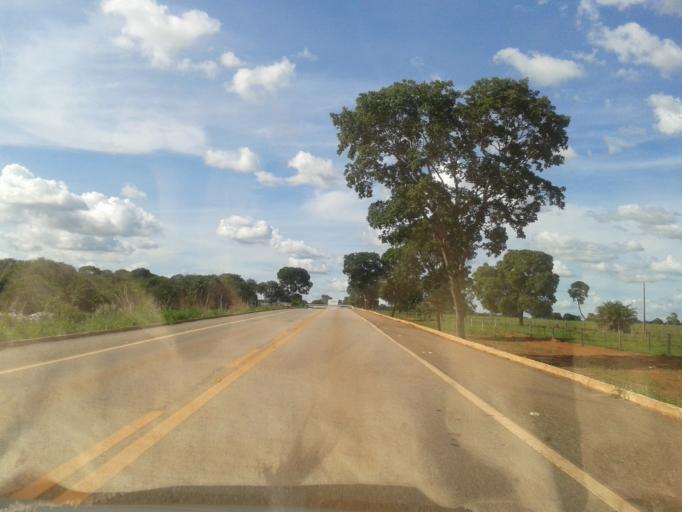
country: BR
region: Goias
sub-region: Mozarlandia
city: Mozarlandia
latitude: -15.1116
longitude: -50.6068
